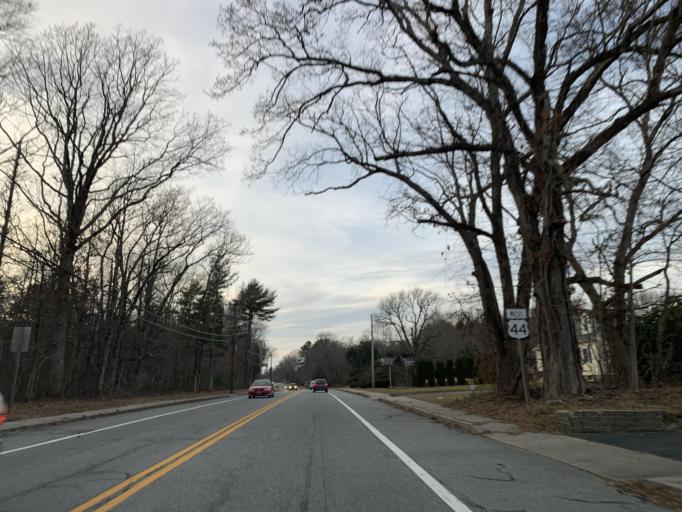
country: US
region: Rhode Island
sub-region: Providence County
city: Chepachet
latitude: 41.9176
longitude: -71.6816
